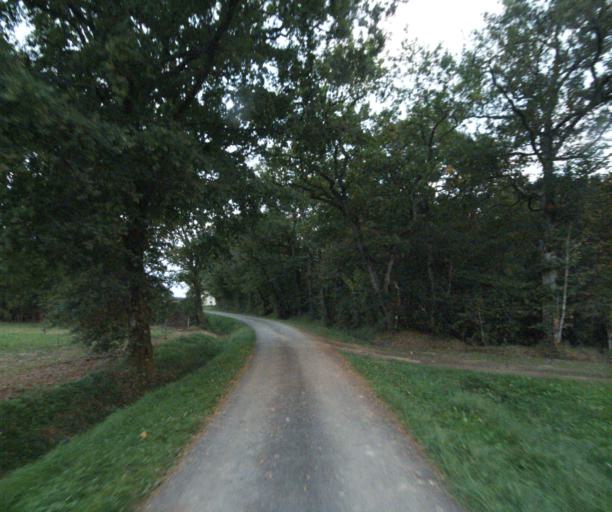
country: FR
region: Midi-Pyrenees
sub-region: Departement du Gers
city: Montreal
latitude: 43.9549
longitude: 0.1175
